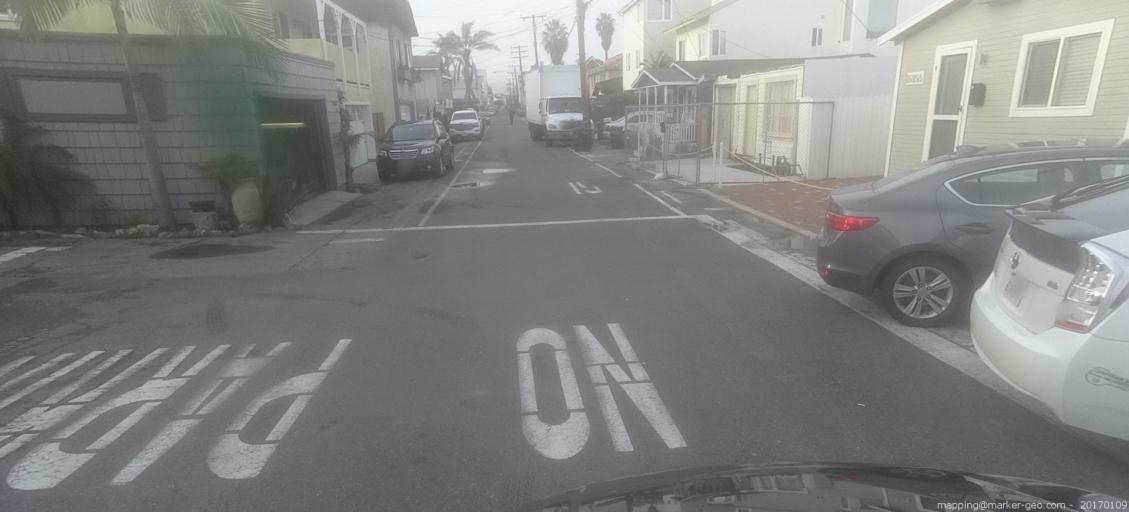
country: US
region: California
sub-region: Orange County
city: Seal Beach
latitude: 33.7176
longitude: -118.0689
